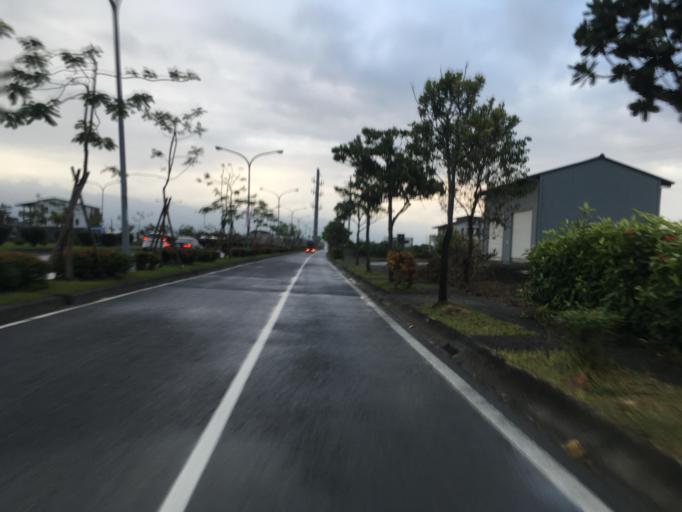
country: TW
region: Taiwan
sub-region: Yilan
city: Yilan
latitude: 24.7285
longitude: 121.7721
